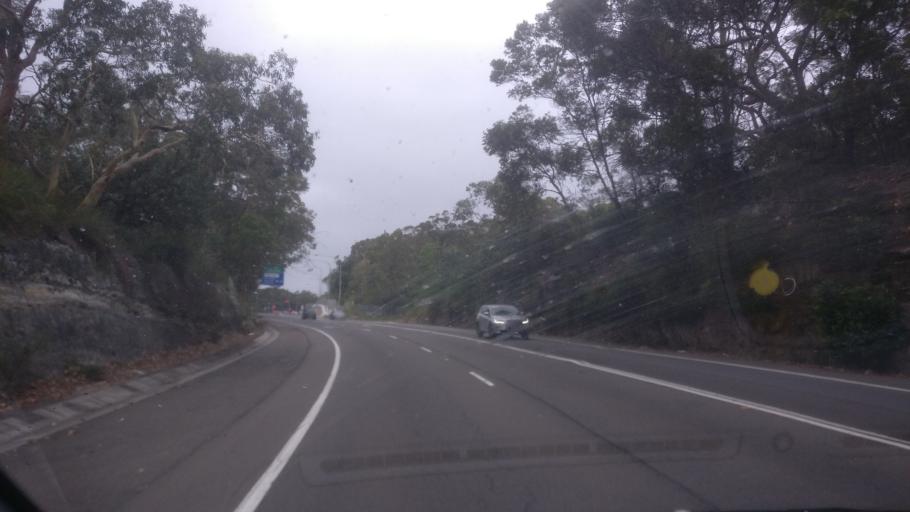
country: AU
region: New South Wales
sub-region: Warringah
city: Allambie Heights
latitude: -33.7465
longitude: 151.2344
